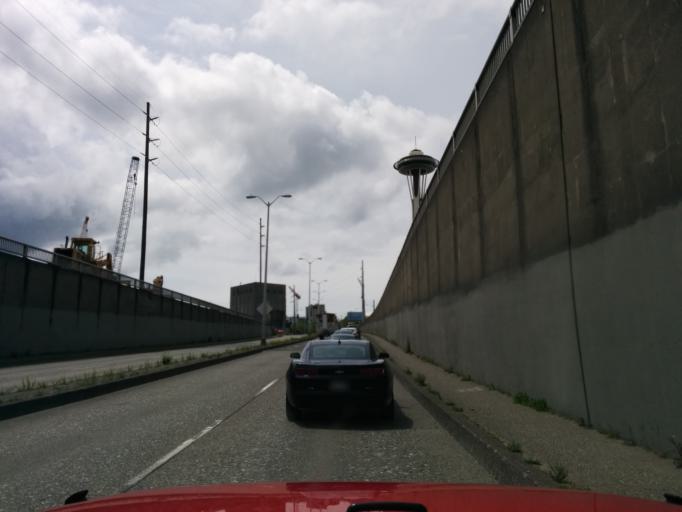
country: US
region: Washington
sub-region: King County
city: Seattle
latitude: 47.6237
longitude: -122.3440
